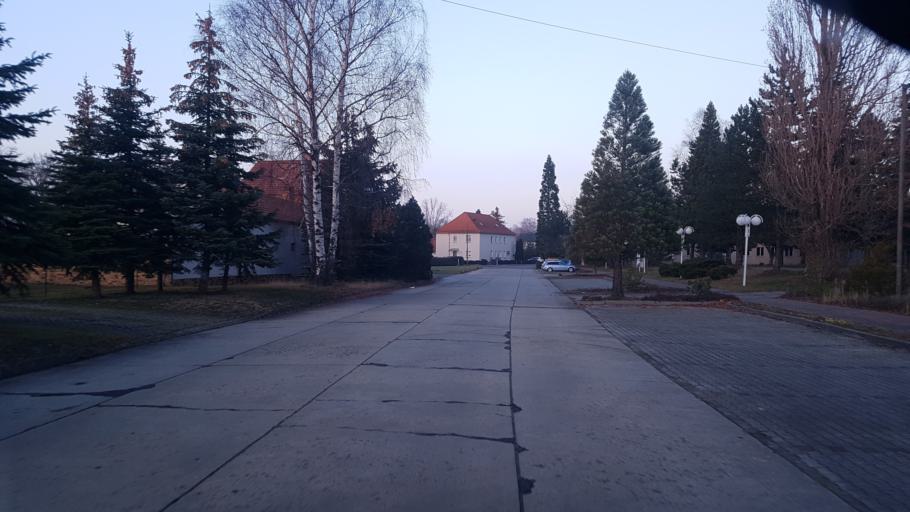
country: DE
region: Brandenburg
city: Lauchhammer
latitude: 51.4780
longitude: 13.7415
